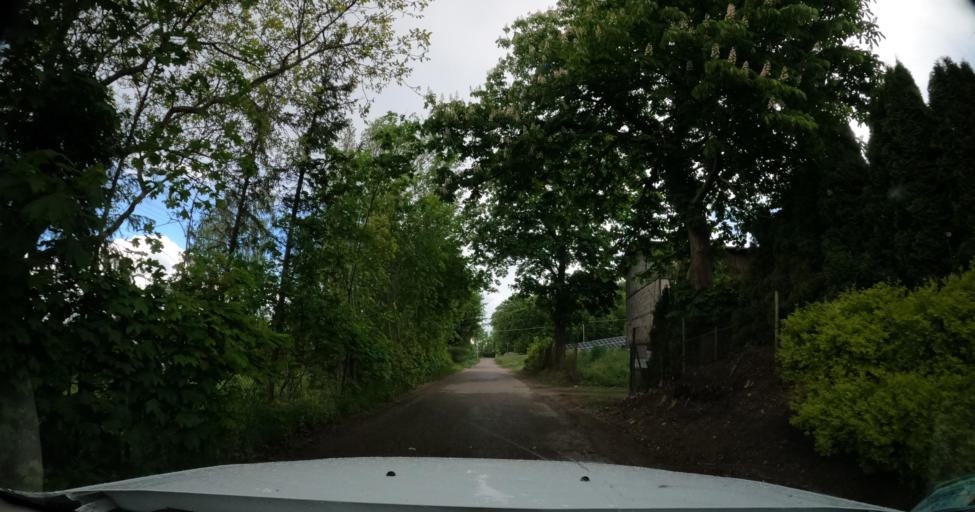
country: PL
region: Pomeranian Voivodeship
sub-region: Powiat kartuski
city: Garcz
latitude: 54.3422
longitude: 18.1454
